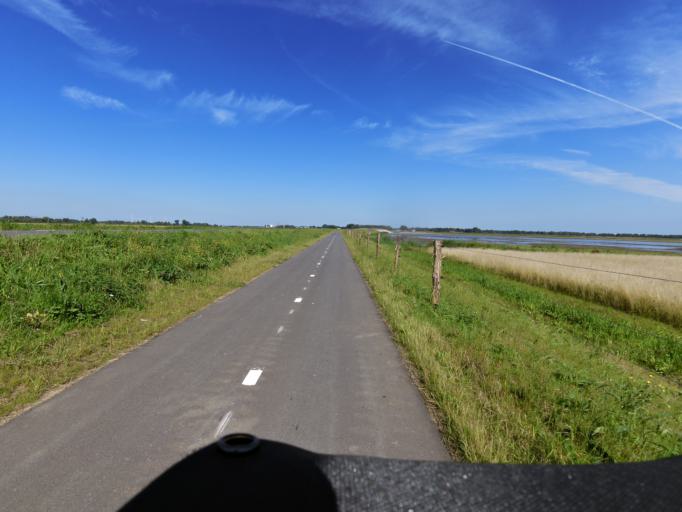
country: NL
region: South Holland
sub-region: Gemeente Hardinxveld-Giessendam
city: Neder-Hardinxveld
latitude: 51.7941
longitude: 4.8453
